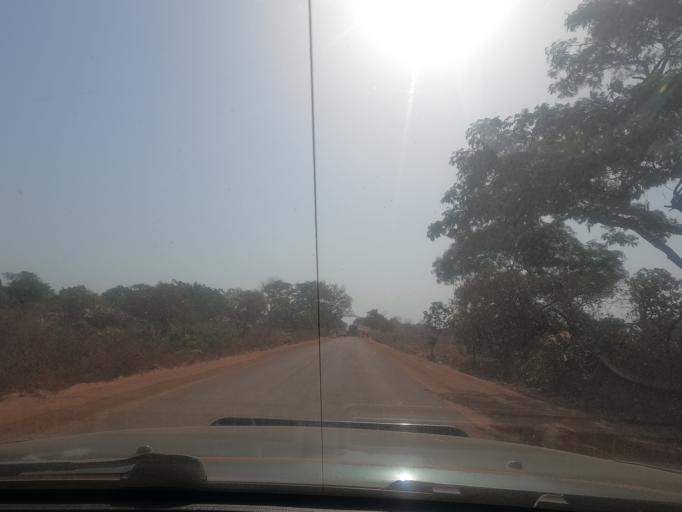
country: GW
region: Oio
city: Mansoa
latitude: 12.0048
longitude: -15.4231
